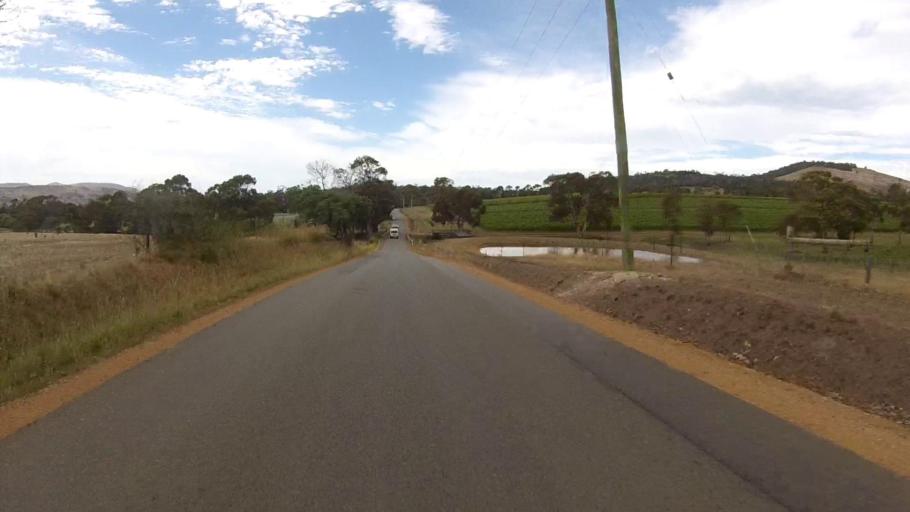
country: AU
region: Tasmania
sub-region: Clarence
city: Lindisfarne
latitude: -42.7605
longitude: 147.3878
